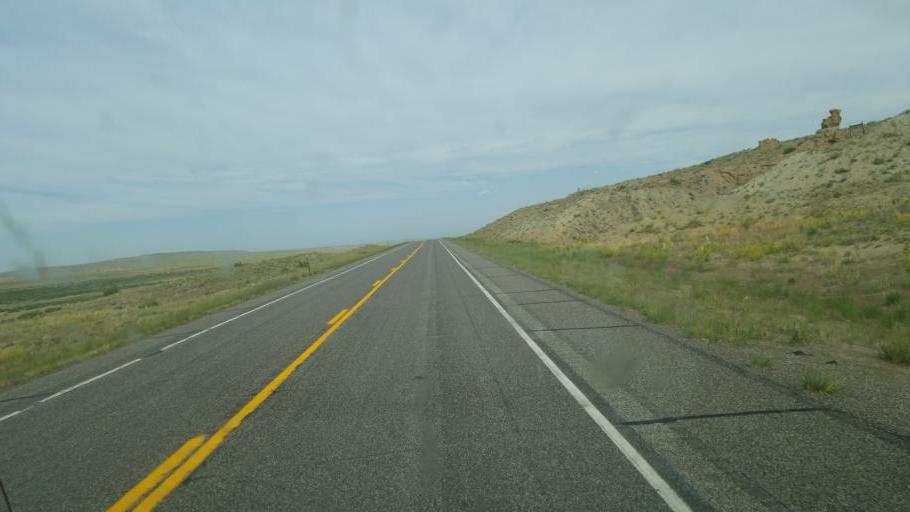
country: US
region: Wyoming
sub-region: Fremont County
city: Riverton
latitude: 43.2210
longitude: -107.9988
